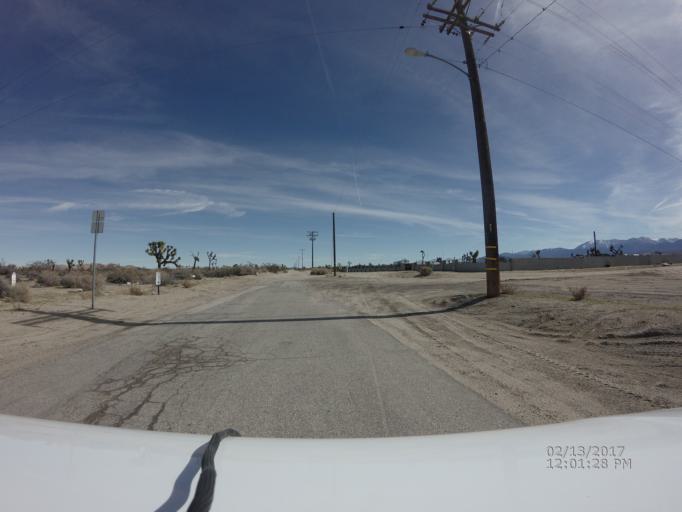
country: US
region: California
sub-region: Los Angeles County
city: Littlerock
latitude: 34.5579
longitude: -117.9233
